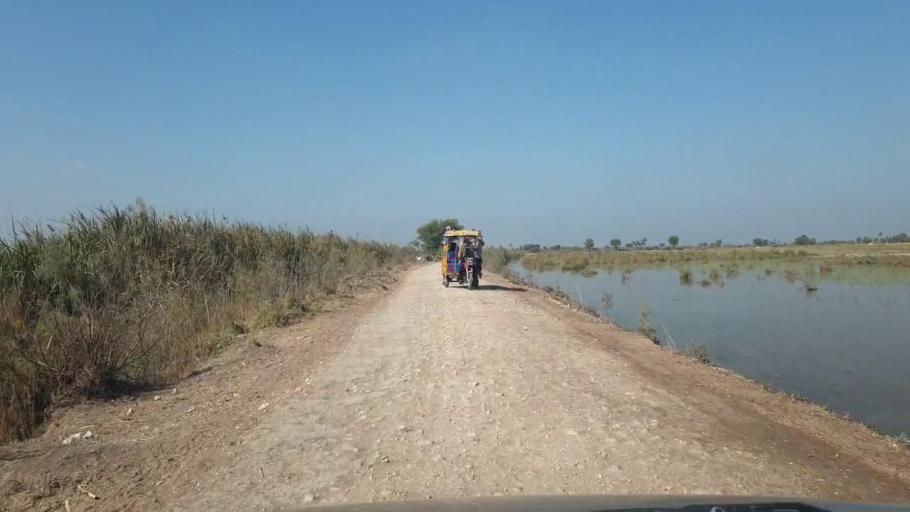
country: PK
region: Sindh
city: Bhit Shah
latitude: 25.8750
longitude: 68.5289
